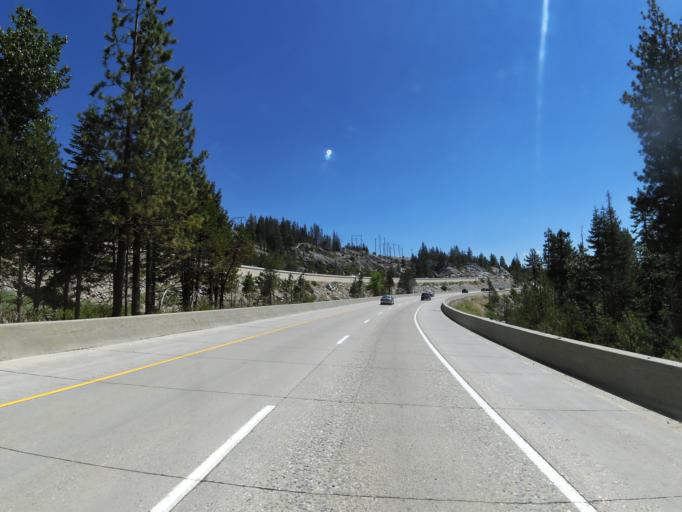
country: US
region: California
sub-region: Nevada County
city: Truckee
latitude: 39.3133
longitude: -120.5141
